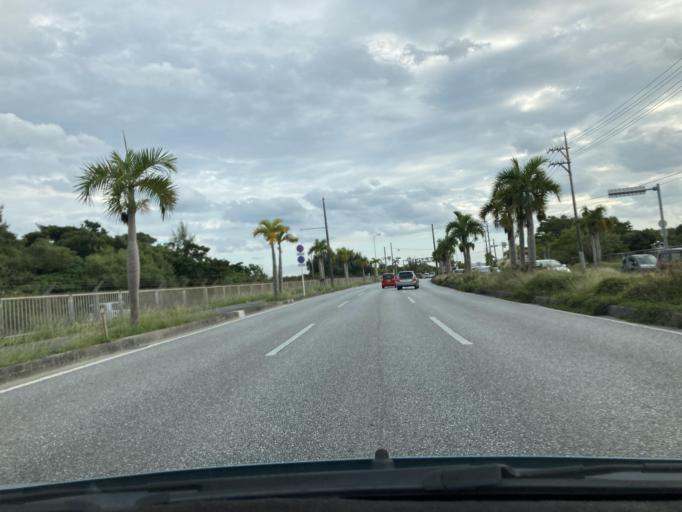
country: JP
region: Okinawa
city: Chatan
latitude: 26.3514
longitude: 127.7467
